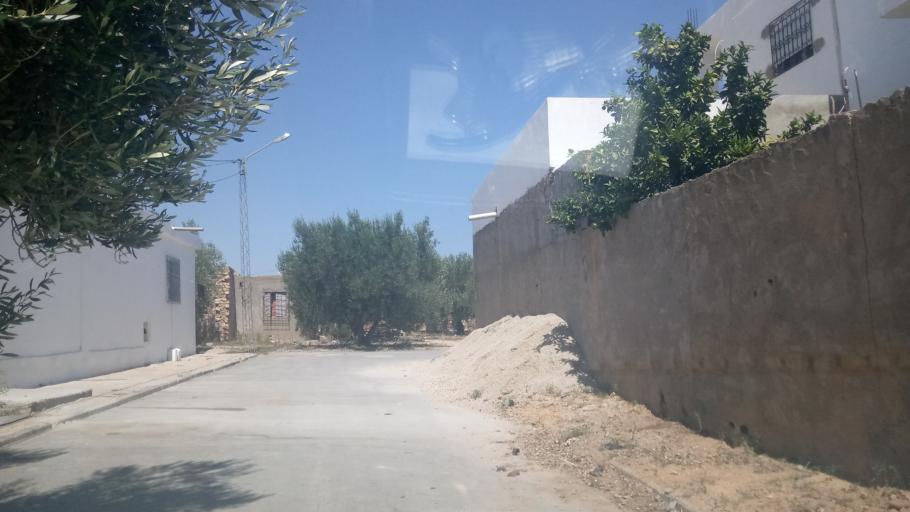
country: TN
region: Al Qayrawan
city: Sbikha
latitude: 36.1179
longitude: 10.0886
